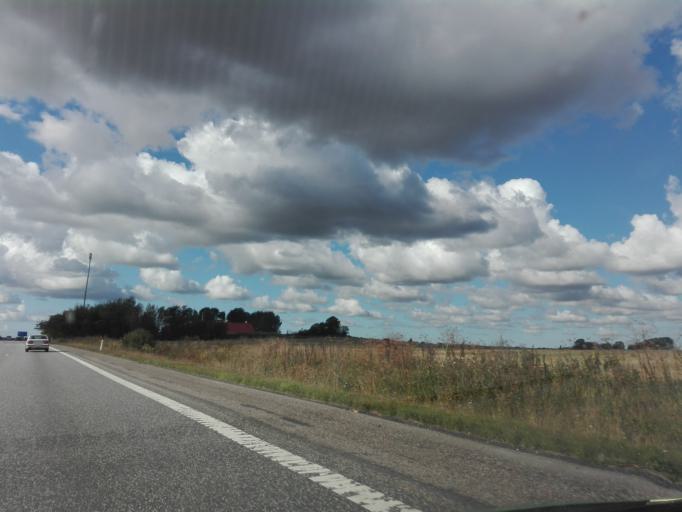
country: DK
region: North Denmark
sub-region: Mariagerfjord Kommune
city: Hobro
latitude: 56.5773
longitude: 9.8331
